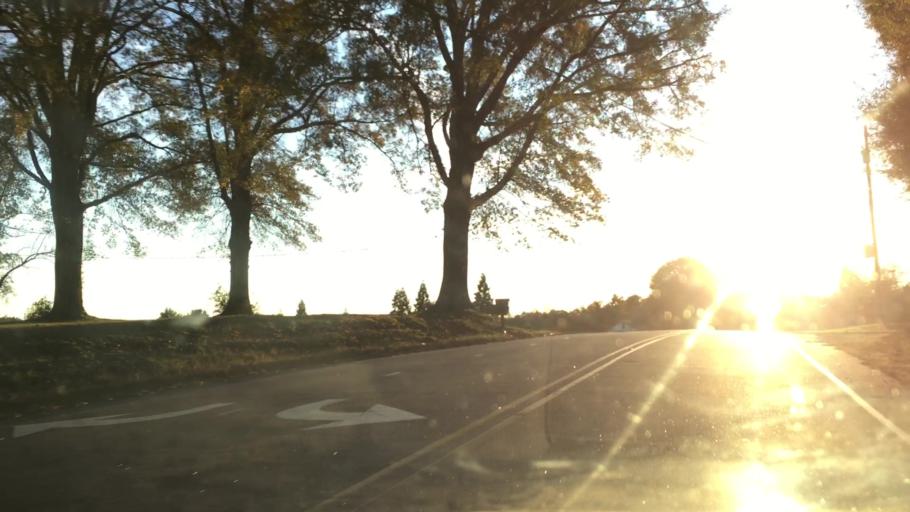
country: US
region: North Carolina
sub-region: Iredell County
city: Mooresville
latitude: 35.5473
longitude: -80.7721
